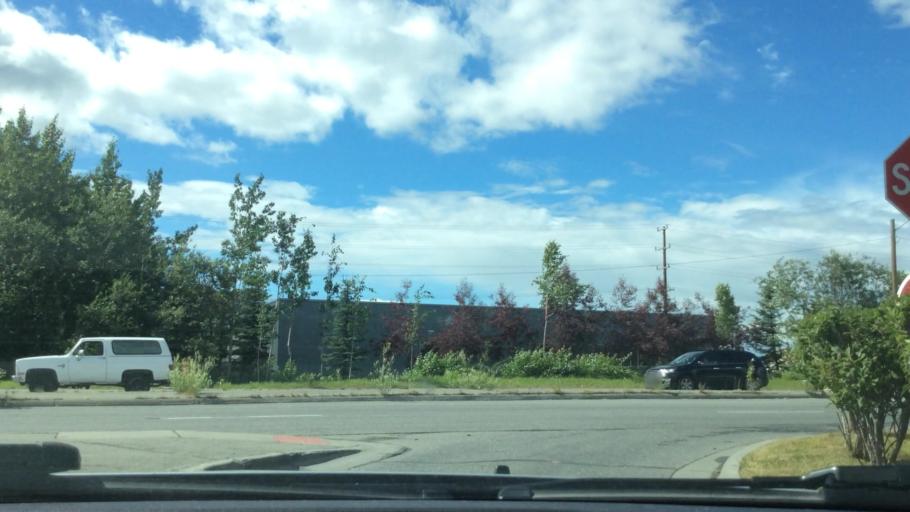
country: US
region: Alaska
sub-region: Anchorage Municipality
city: Anchorage
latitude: 61.2109
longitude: -149.8079
